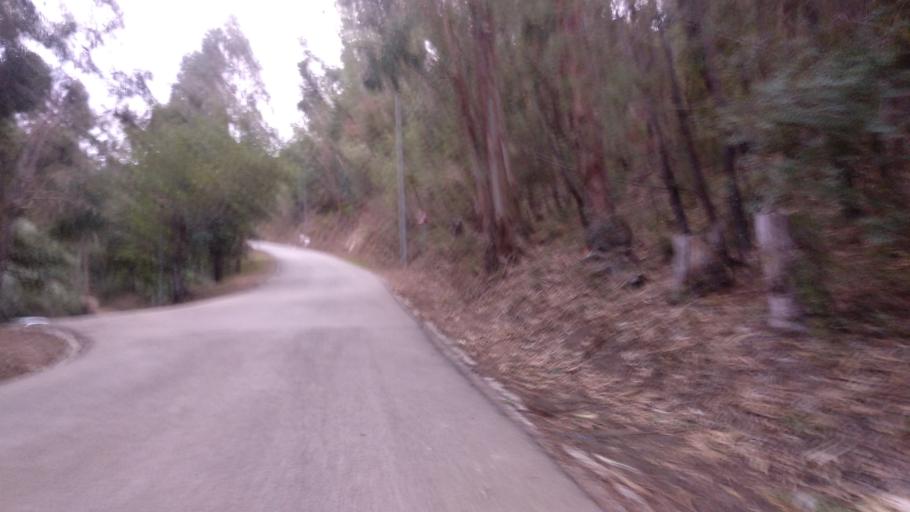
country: PT
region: Faro
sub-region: Sao Bras de Alportel
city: Sao Bras de Alportel
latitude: 37.1835
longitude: -7.9138
